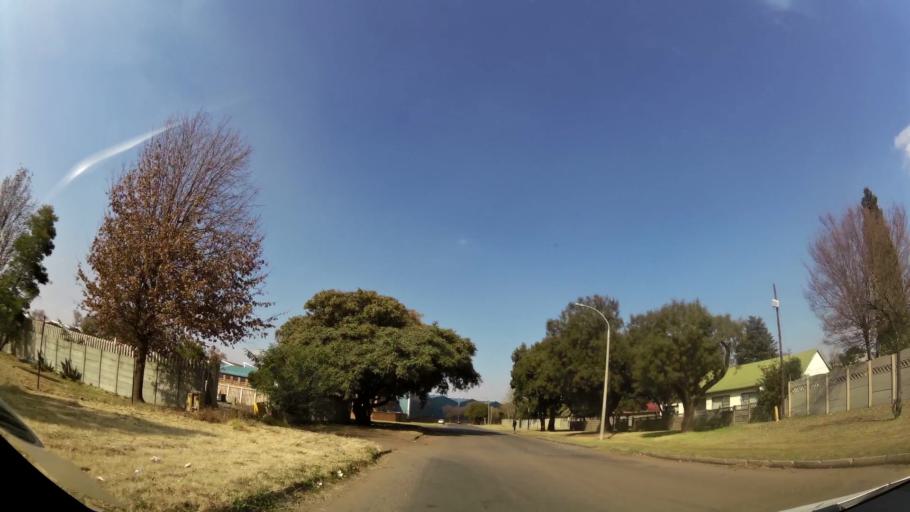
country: ZA
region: Gauteng
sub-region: Ekurhuleni Metropolitan Municipality
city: Boksburg
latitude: -26.1924
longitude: 28.2117
